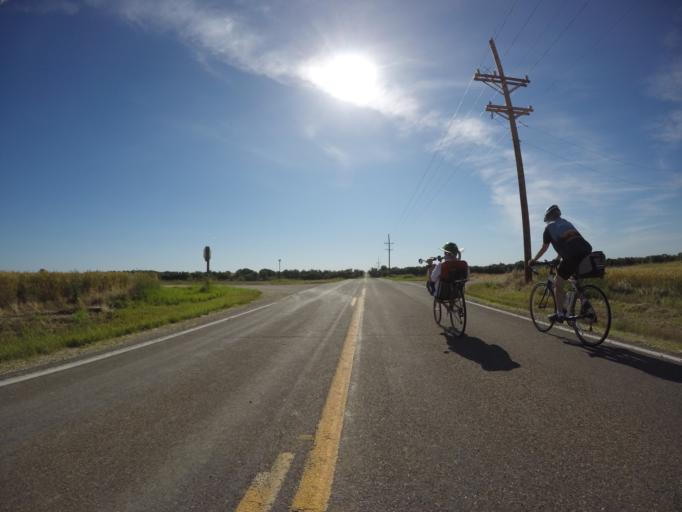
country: US
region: Kansas
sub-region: Mitchell County
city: Beloit
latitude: 39.6394
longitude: -97.9507
